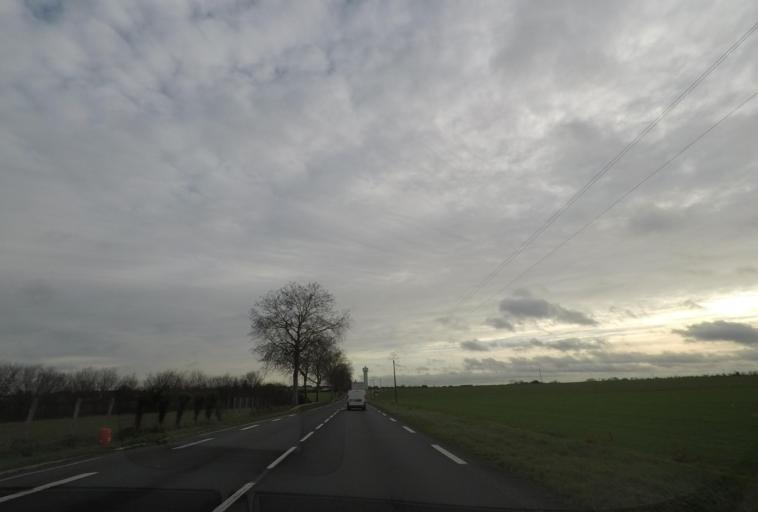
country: FR
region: Centre
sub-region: Departement du Loir-et-Cher
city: Sarge-sur-Braye
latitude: 47.9018
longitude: 0.9166
